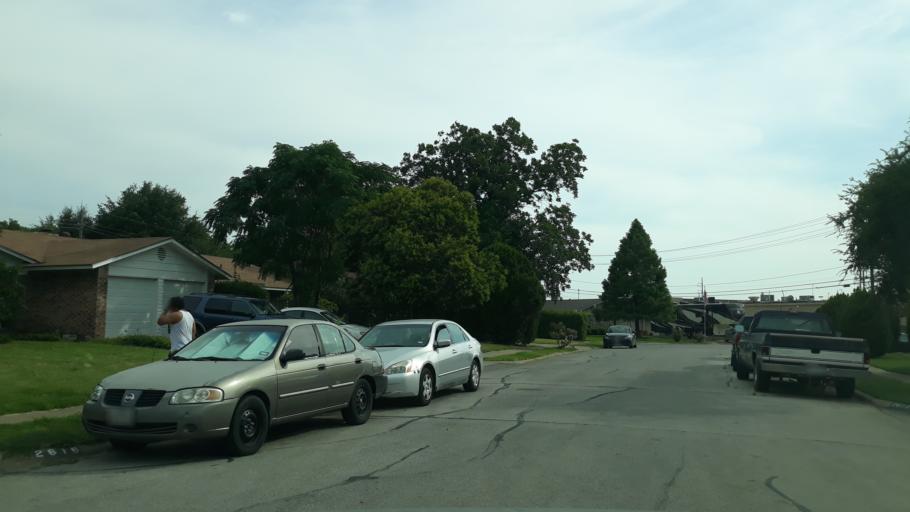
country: US
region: Texas
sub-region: Dallas County
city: Irving
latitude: 32.8427
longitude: -96.9908
